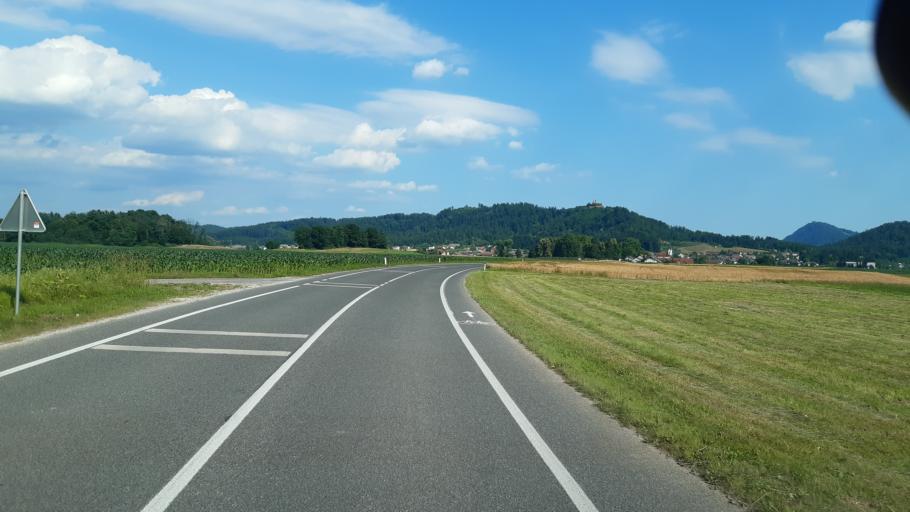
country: SI
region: Medvode
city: Zgornje Pirnice
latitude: 46.1788
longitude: 14.4220
